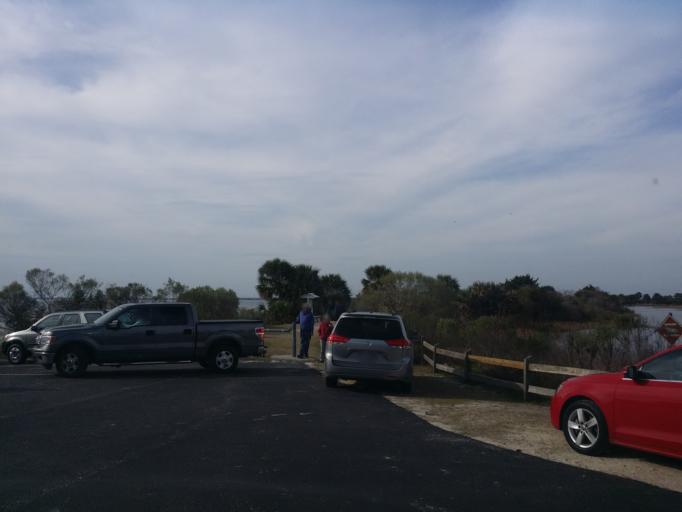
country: US
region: Florida
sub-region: Wakulla County
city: Crawfordville
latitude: 30.0744
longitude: -84.1799
